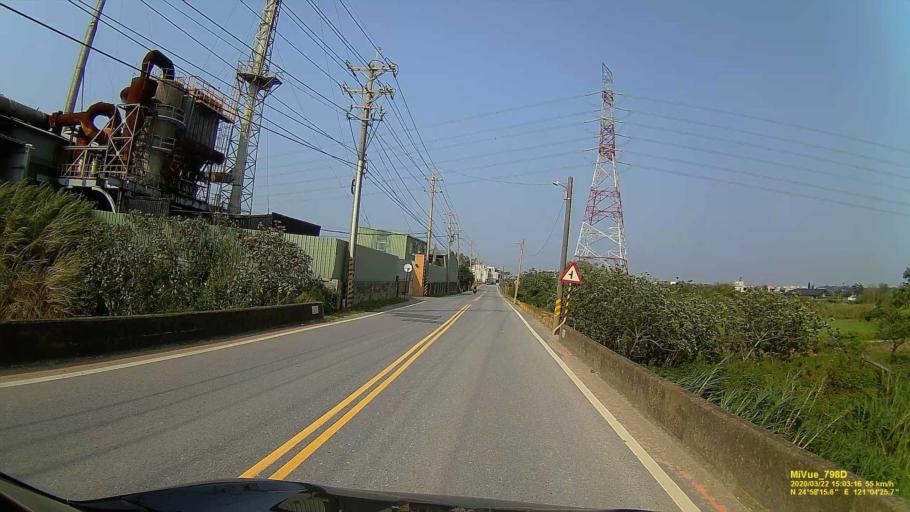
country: TW
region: Taiwan
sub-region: Hsinchu
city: Zhubei
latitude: 24.9713
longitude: 121.0741
